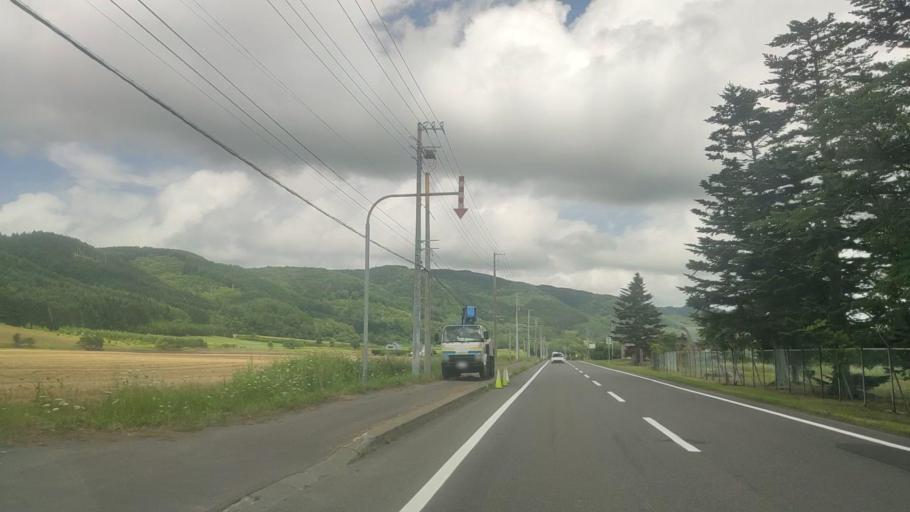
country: JP
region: Hokkaido
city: Date
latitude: 42.5701
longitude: 140.9247
